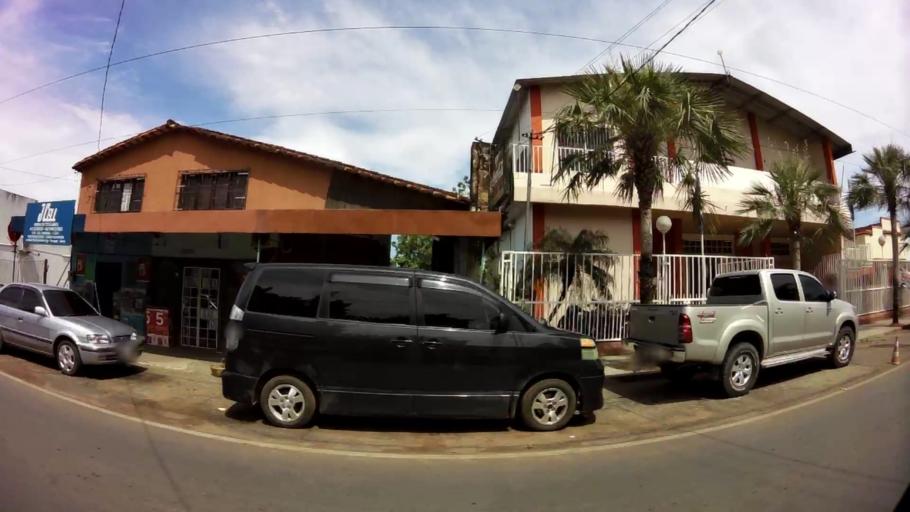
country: PY
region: Central
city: Limpio
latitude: -25.1674
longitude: -57.4744
